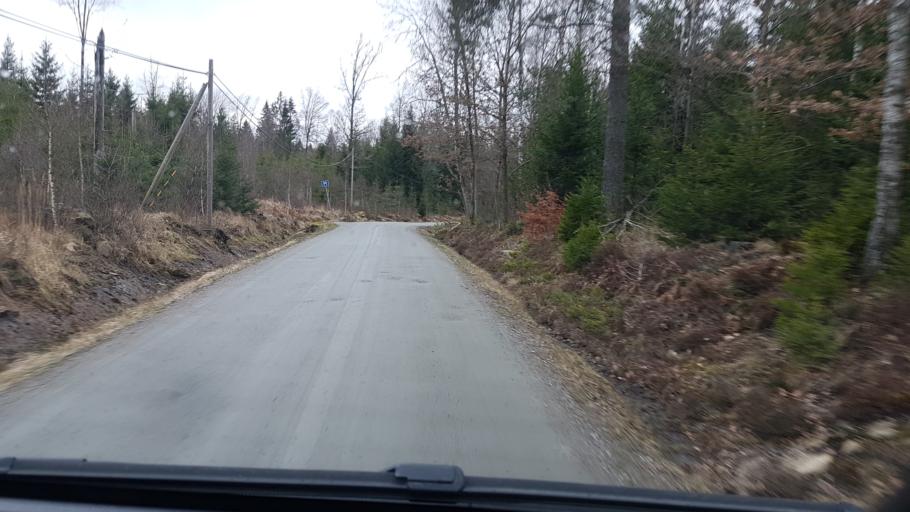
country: SE
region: Vaestra Goetaland
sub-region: Lerums Kommun
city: Stenkullen
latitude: 57.7995
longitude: 12.3837
